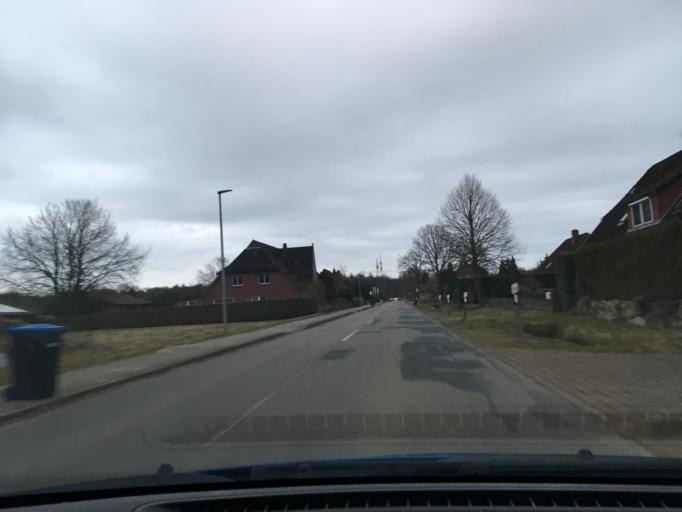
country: DE
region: Lower Saxony
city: Brietlingen
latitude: 53.3283
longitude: 10.4552
